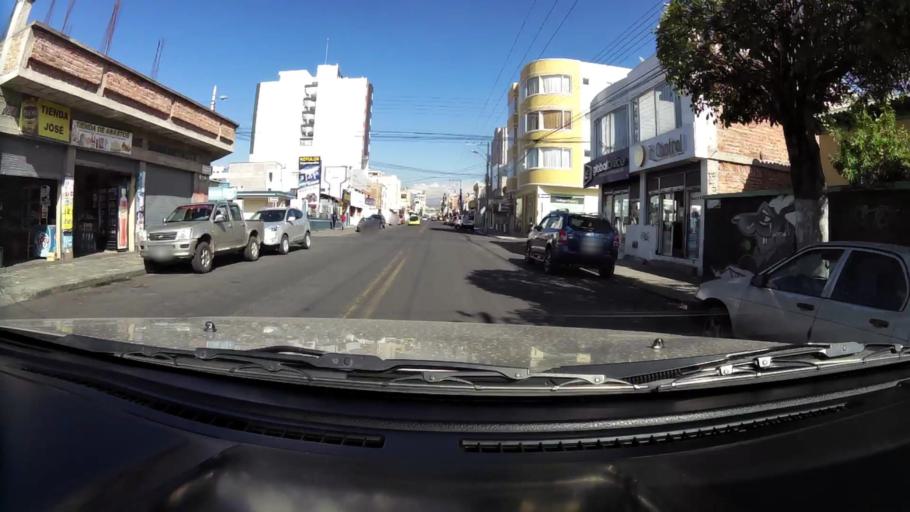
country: EC
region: Chimborazo
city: Riobamba
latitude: -1.6656
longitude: -78.6559
